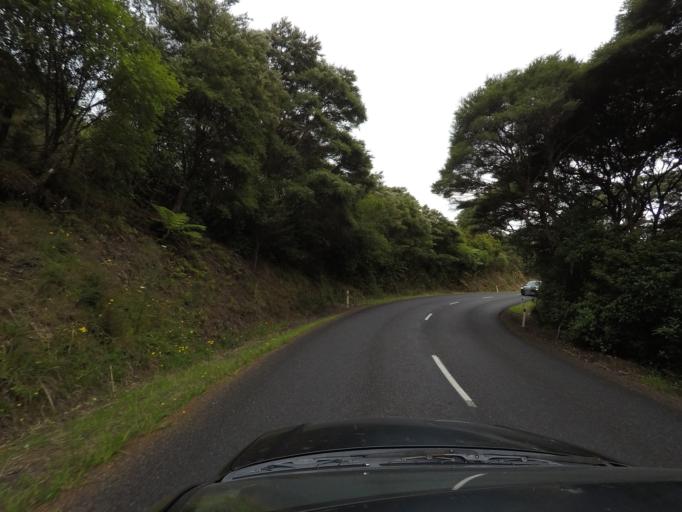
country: NZ
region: Waikato
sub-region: Waikato District
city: Raglan
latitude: -37.8247
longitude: 174.8146
